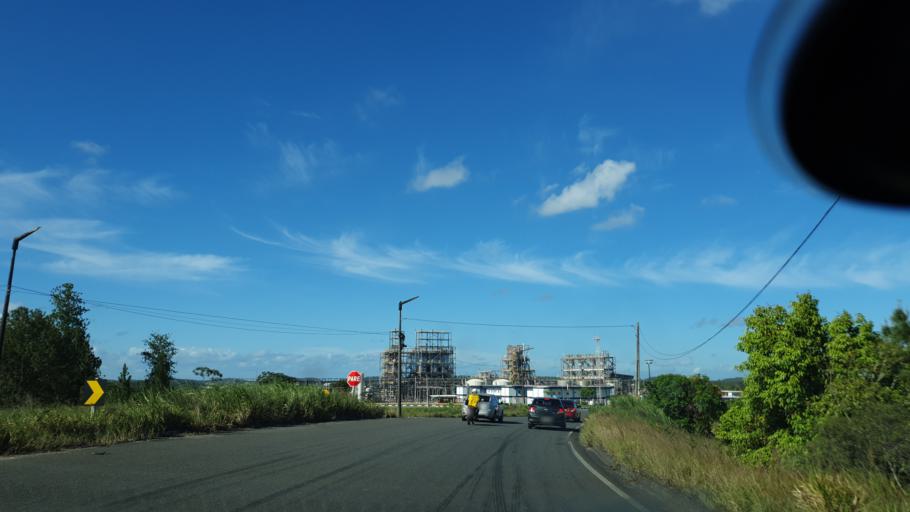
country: BR
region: Bahia
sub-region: Camacari
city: Camacari
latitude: -12.6603
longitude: -38.3017
